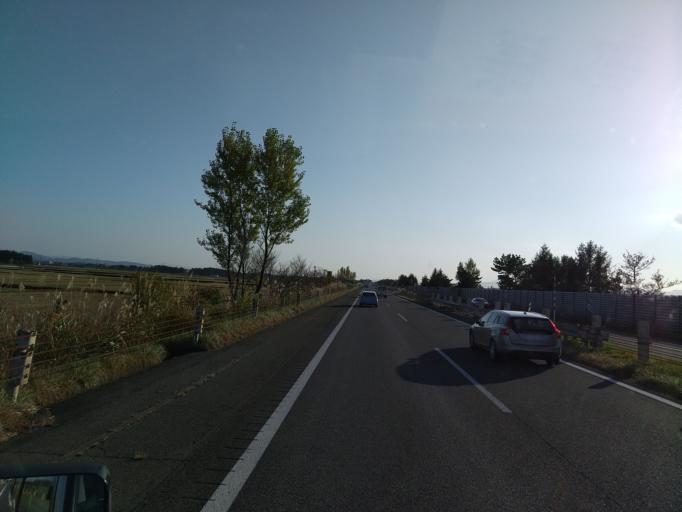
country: JP
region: Iwate
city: Hanamaki
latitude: 39.4380
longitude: 141.1075
